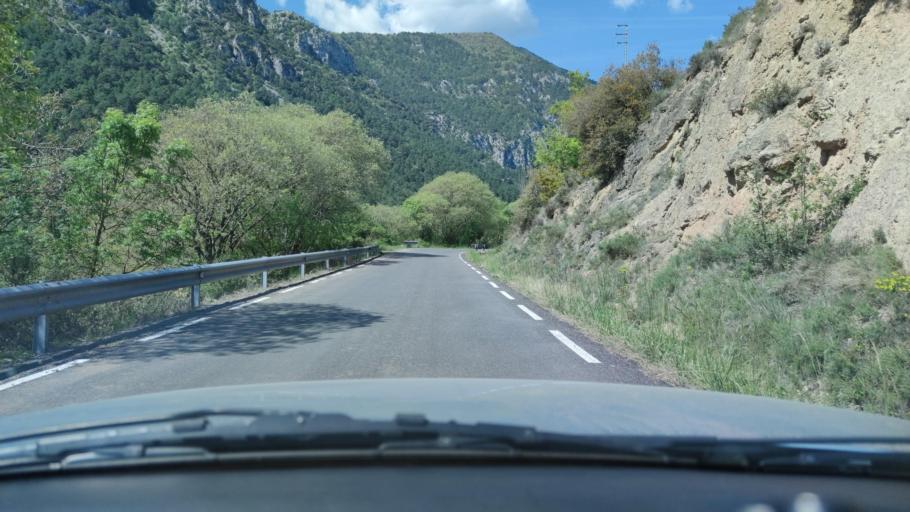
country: ES
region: Catalonia
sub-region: Provincia de Lleida
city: Coll de Nargo
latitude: 42.2922
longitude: 1.3388
